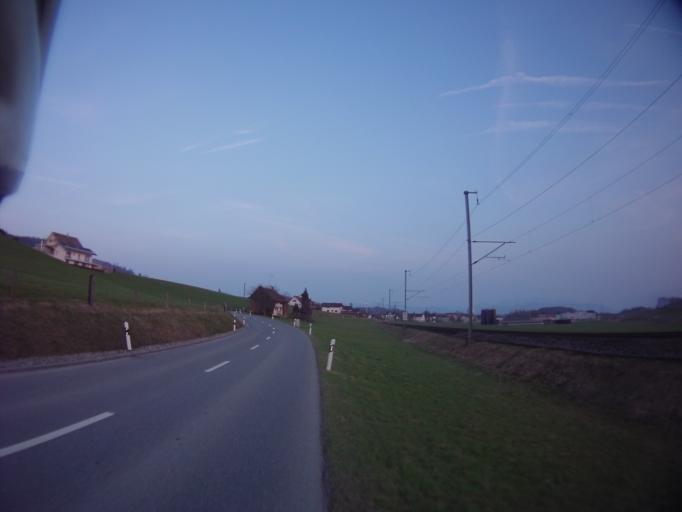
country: CH
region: Zurich
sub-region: Bezirk Affoltern
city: Mettmenstetten
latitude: 47.2510
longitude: 8.4510
